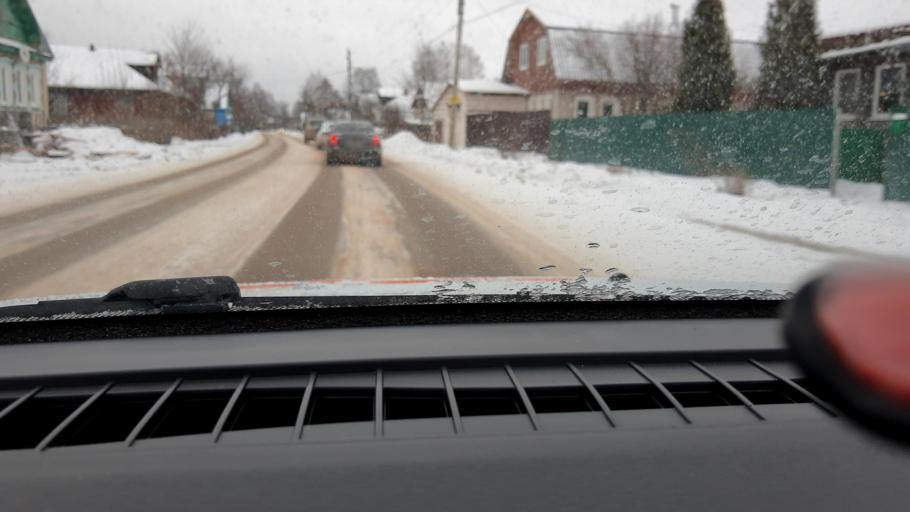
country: RU
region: Nizjnij Novgorod
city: Afonino
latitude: 56.3183
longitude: 44.1726
